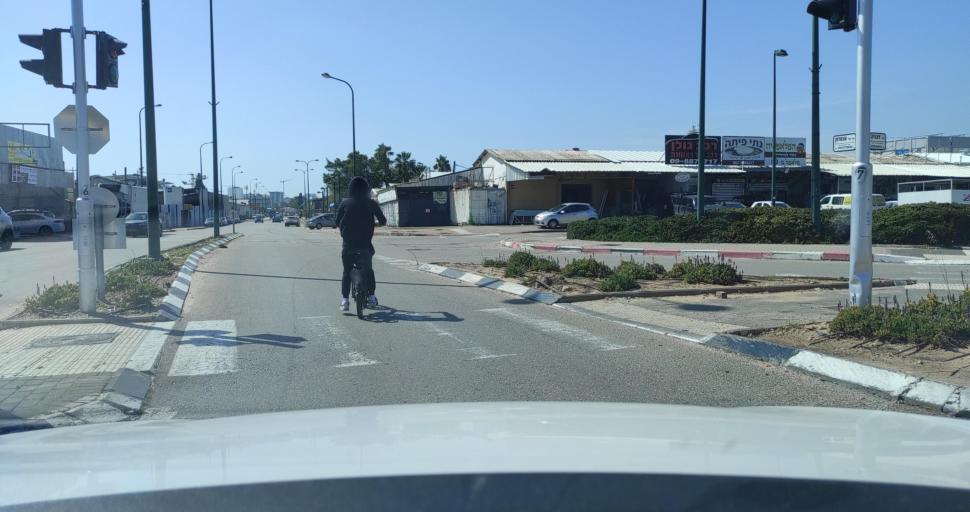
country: IL
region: Central District
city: Bet Yizhaq
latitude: 32.3197
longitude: 34.8825
